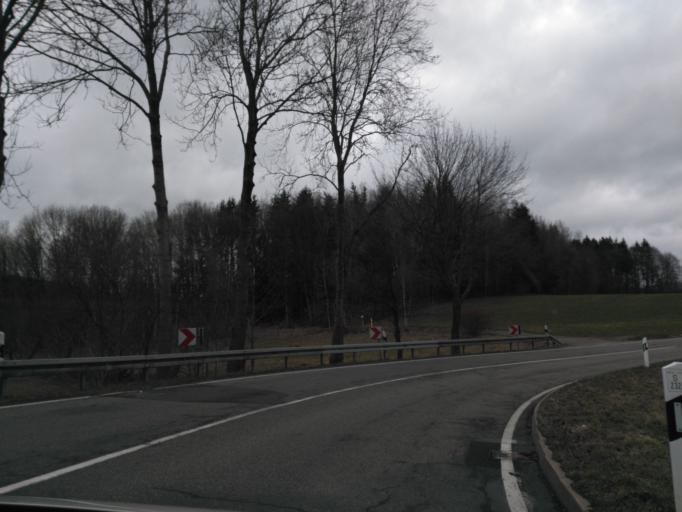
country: DE
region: Saxony
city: Venusberg
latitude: 50.7175
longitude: 12.9959
